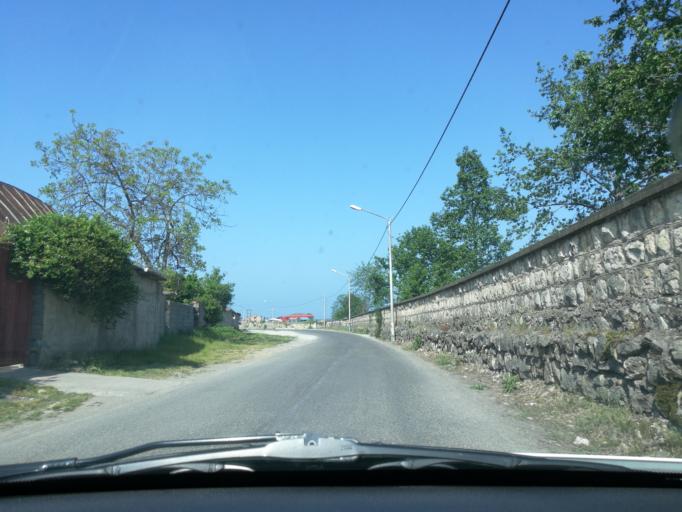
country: IR
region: Mazandaran
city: Chalus
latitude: 36.6575
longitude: 51.4316
